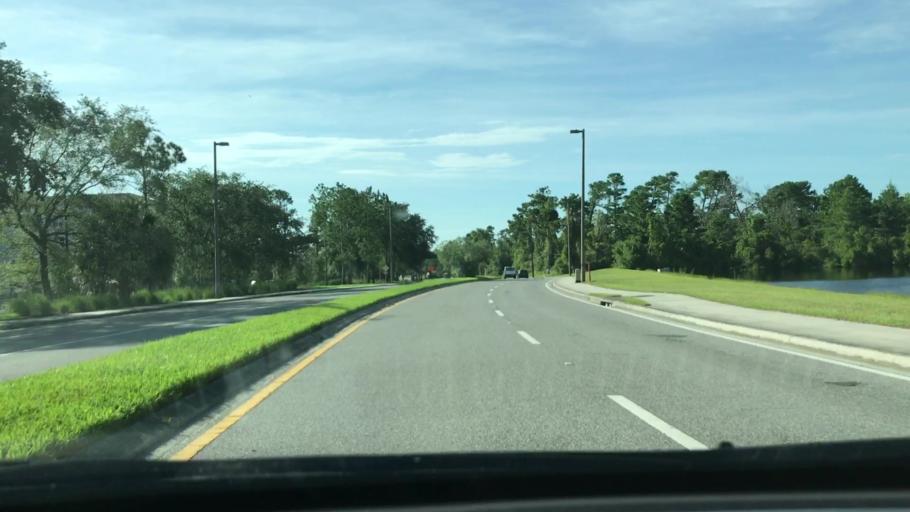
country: US
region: Florida
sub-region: Orange County
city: Williamsburg
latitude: 28.3949
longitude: -81.4700
